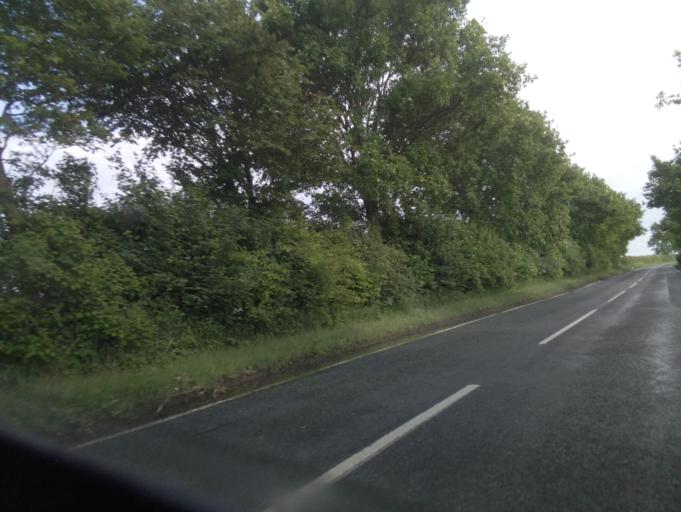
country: GB
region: England
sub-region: Lincolnshire
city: Great Gonerby
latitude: 53.0439
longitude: -0.6456
